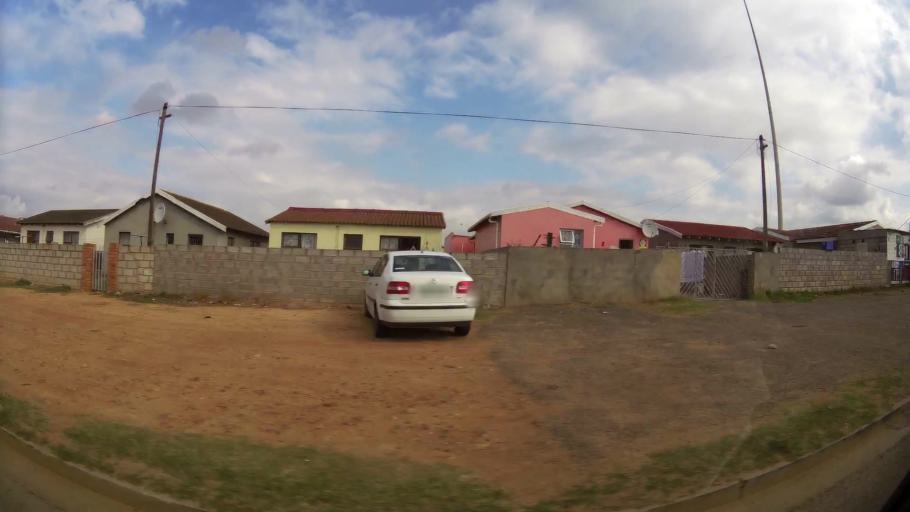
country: ZA
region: Eastern Cape
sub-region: Nelson Mandela Bay Metropolitan Municipality
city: Port Elizabeth
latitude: -33.8159
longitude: 25.5934
